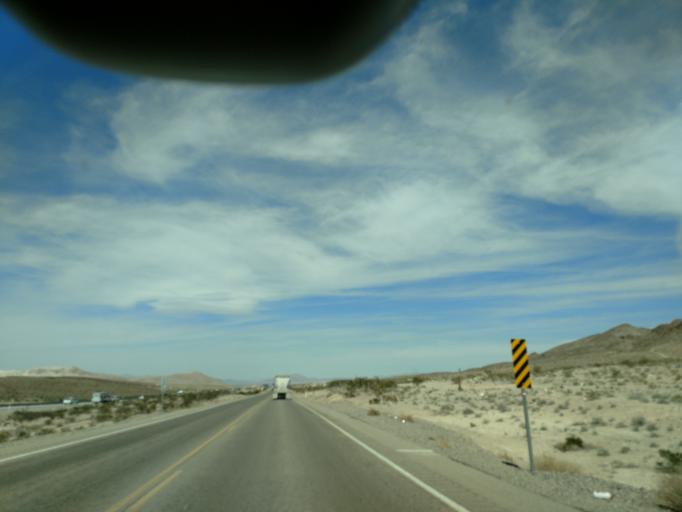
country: US
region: Nevada
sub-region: Clark County
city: Enterprise
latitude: 35.8866
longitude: -115.2234
